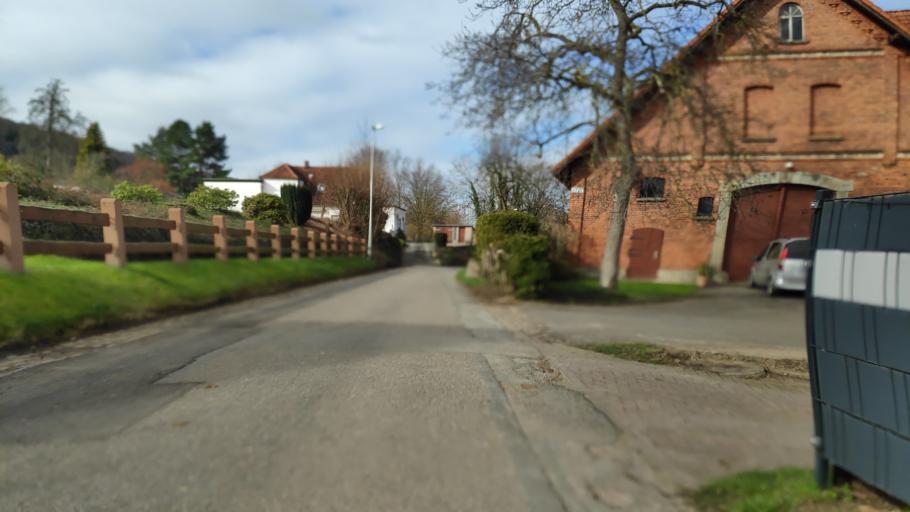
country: DE
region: North Rhine-Westphalia
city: Porta Westfalica
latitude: 52.2586
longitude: 8.8688
